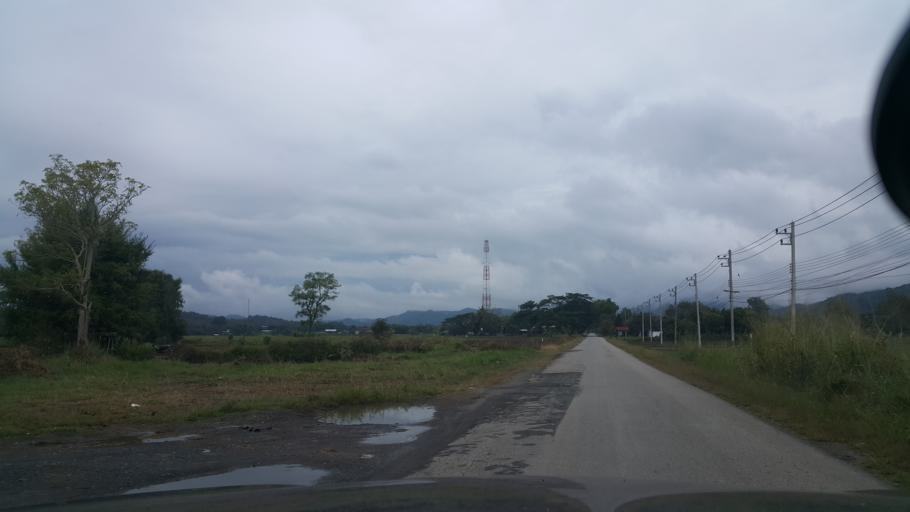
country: TH
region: Chiang Mai
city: Mae On
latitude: 18.7759
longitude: 99.2542
